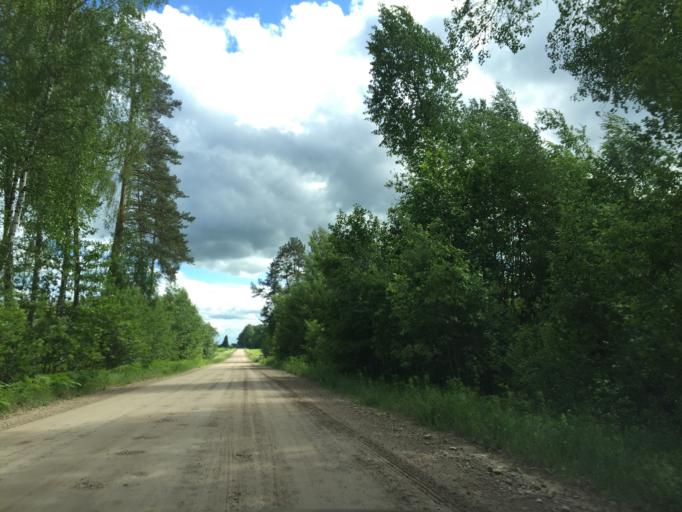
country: LV
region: Vecumnieki
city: Vecumnieki
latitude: 56.4851
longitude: 24.4133
